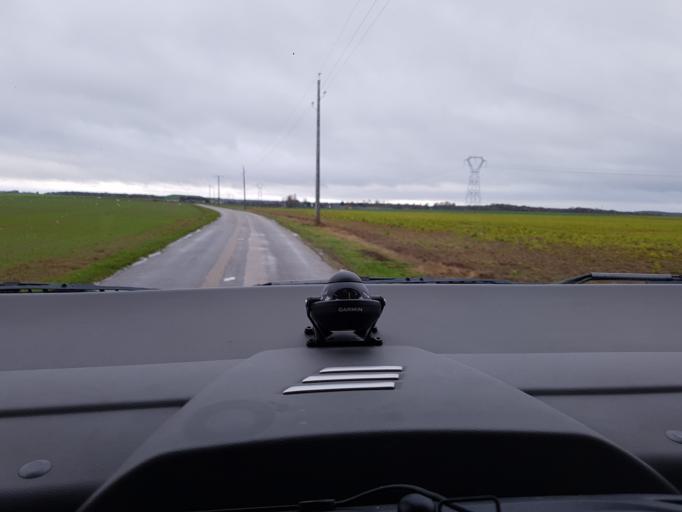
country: FR
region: Haute-Normandie
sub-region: Departement de l'Eure
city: Pont-Saint-Pierre
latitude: 49.2973
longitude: 1.3304
